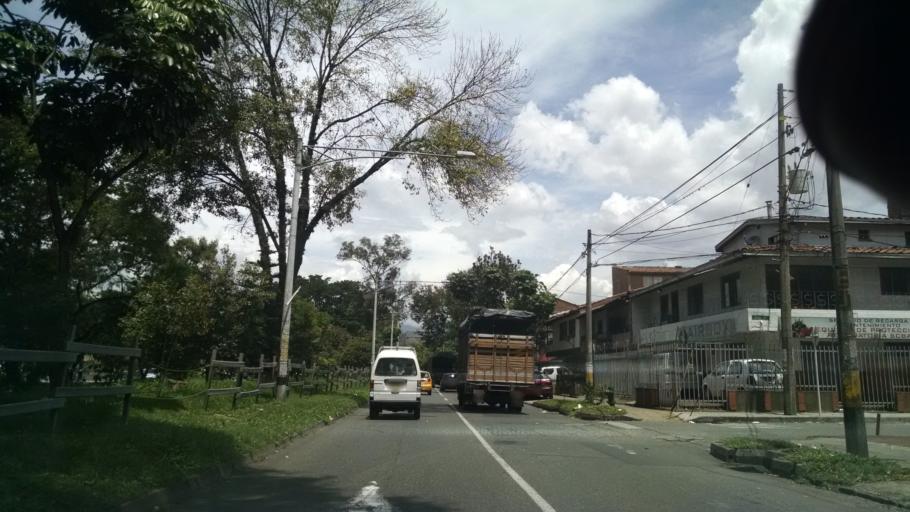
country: CO
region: Antioquia
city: Medellin
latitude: 6.2234
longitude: -75.5840
